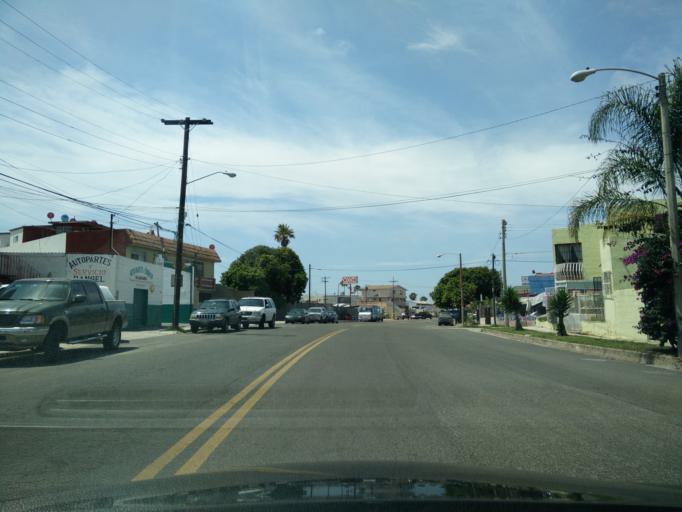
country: MX
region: Baja California
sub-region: Tijuana
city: La Esperanza [Granjas Familiares]
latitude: 32.5106
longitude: -117.1194
